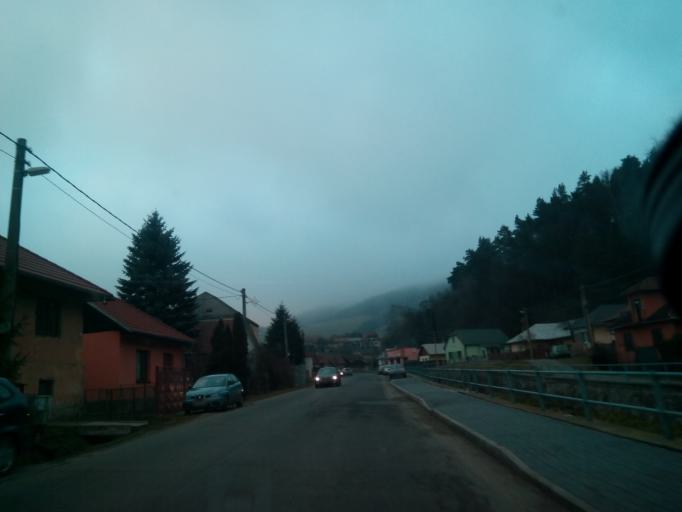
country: SK
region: Kosicky
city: Krompachy
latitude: 48.9247
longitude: 20.9411
